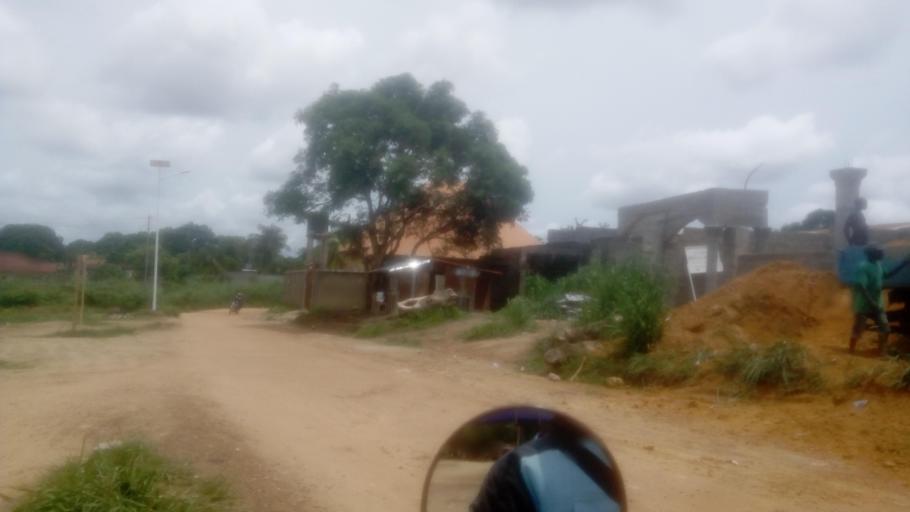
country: SL
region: Southern Province
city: Bo
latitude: 7.9514
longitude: -11.7143
